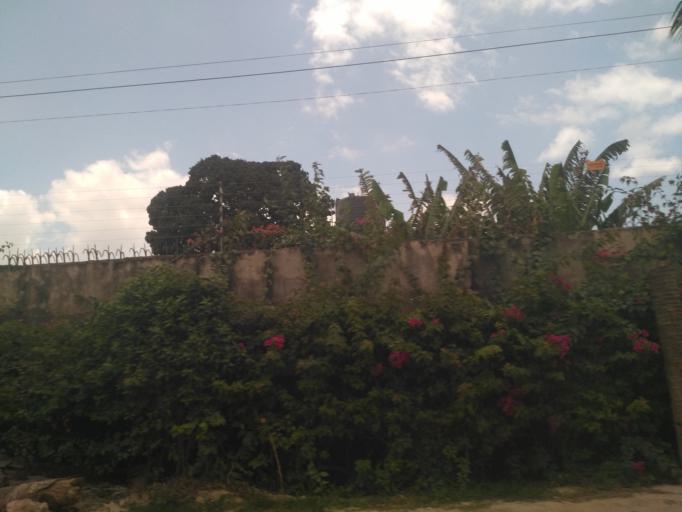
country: TZ
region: Dar es Salaam
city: Dar es Salaam
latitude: -6.8570
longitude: 39.2873
